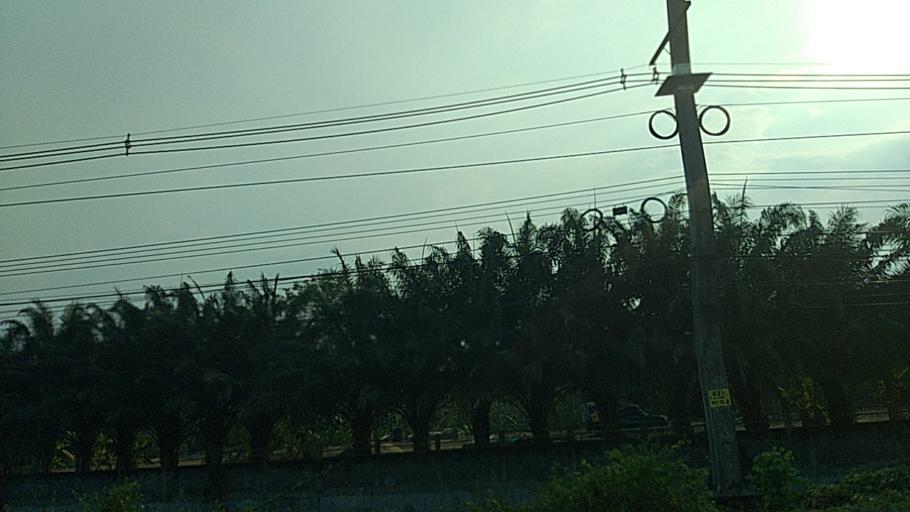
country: TH
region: Nakhon Nayok
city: Nakhon Nayok
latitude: 14.2110
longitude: 101.1775
